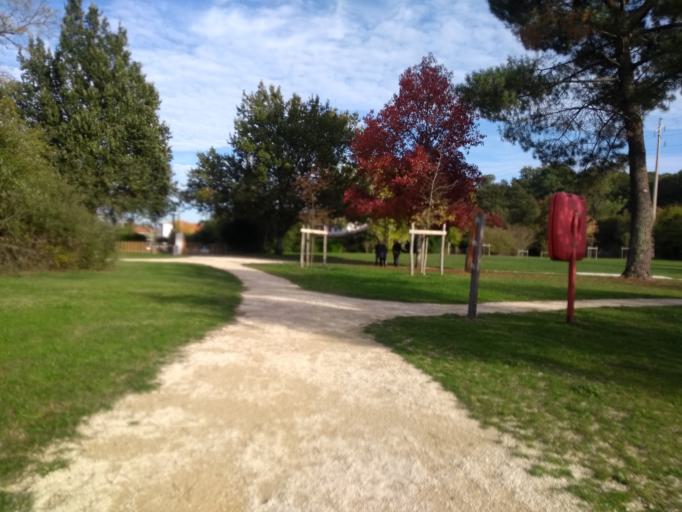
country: FR
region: Aquitaine
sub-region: Departement de la Gironde
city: Pessac
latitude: 44.7923
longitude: -0.6637
